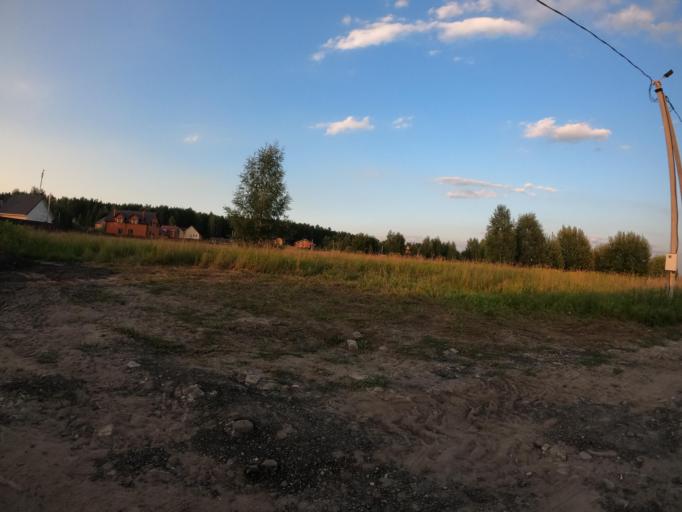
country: RU
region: Moskovskaya
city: Ramenskoye
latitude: 55.5604
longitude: 38.3044
